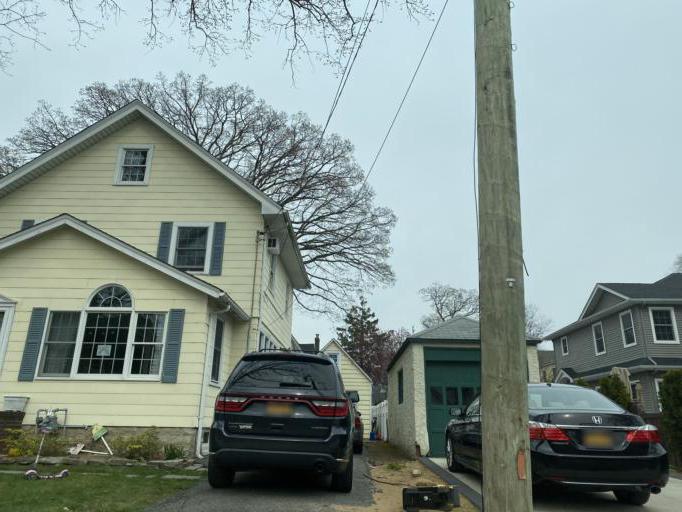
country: US
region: New York
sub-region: Nassau County
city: Bellerose
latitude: 40.7193
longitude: -73.7192
